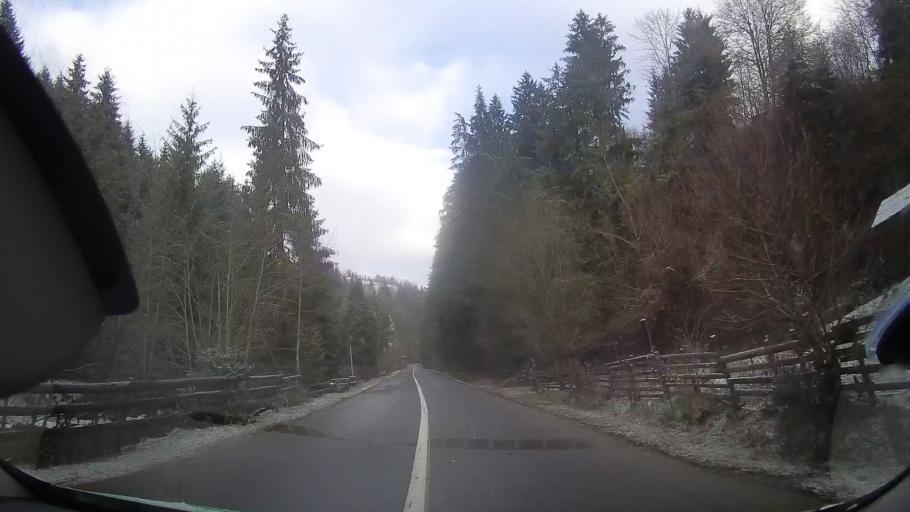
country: RO
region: Alba
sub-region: Comuna Horea
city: Horea
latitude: 46.4844
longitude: 22.9621
